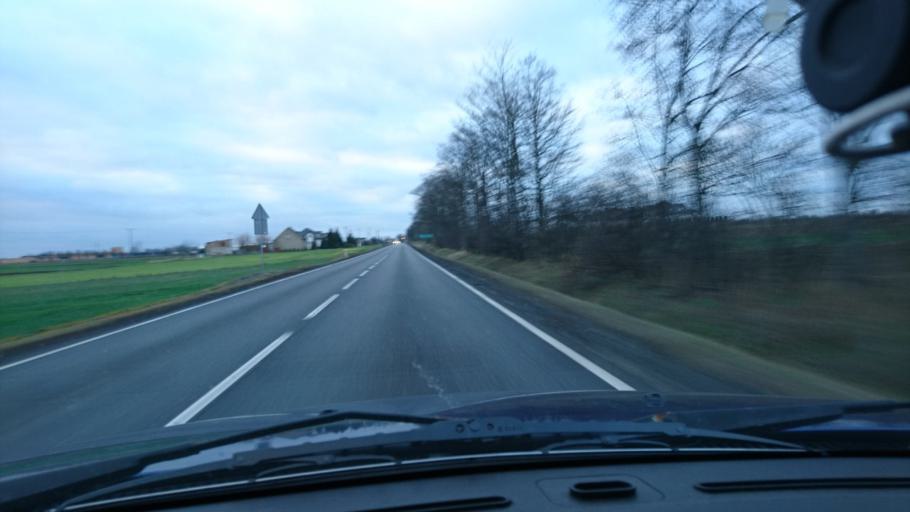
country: PL
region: Greater Poland Voivodeship
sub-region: Powiat kepinski
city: Slupia pod Kepnem
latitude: 51.2358
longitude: 18.0529
